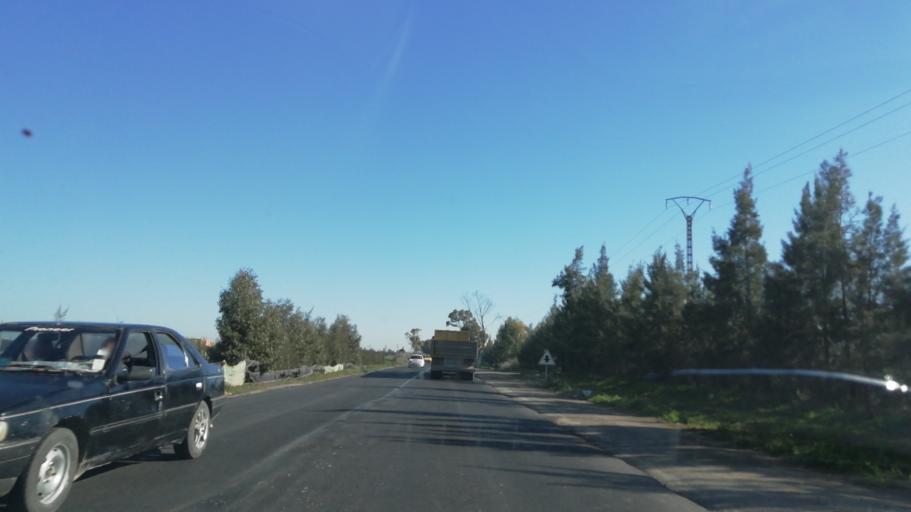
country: DZ
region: Relizane
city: Zemoura
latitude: 35.7571
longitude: 0.6708
